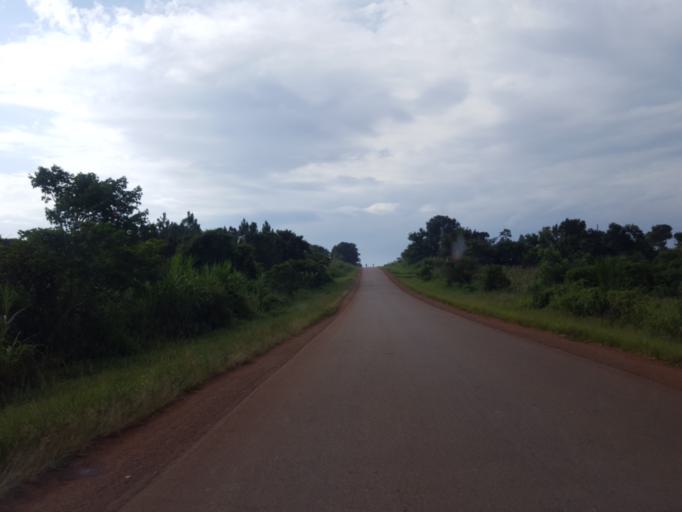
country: UG
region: Western Region
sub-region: Hoima District
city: Hoima
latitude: 1.2489
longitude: 31.5217
